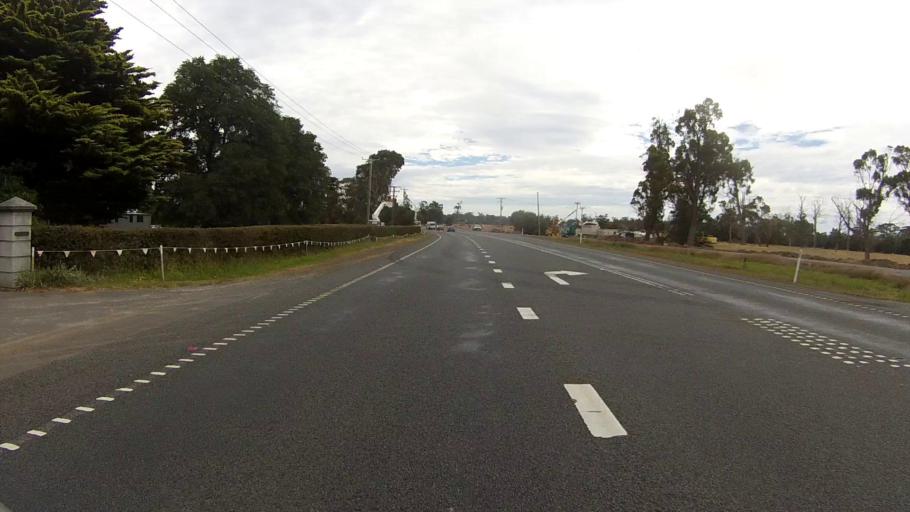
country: AU
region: Tasmania
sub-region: Northern Midlands
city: Evandale
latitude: -41.5995
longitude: 147.2142
